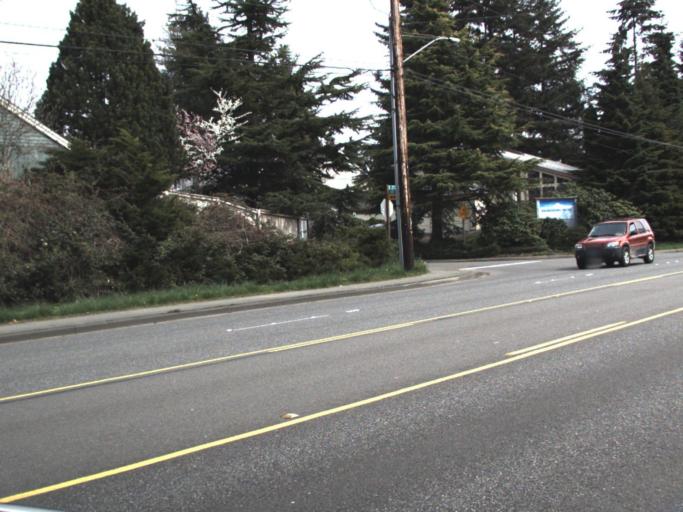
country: US
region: Washington
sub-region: King County
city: Covington
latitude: 47.3580
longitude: -122.1560
